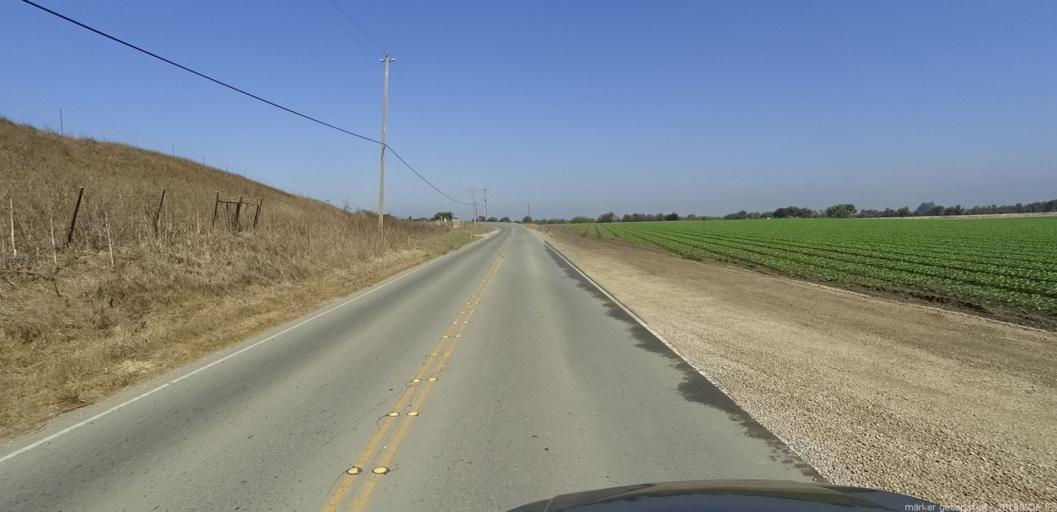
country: US
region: California
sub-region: Monterey County
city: Chualar
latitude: 36.5689
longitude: -121.5695
